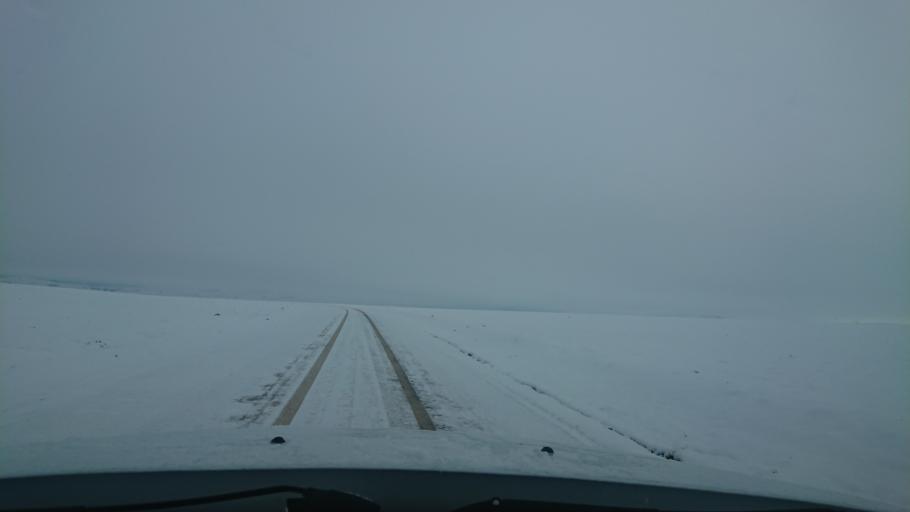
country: TR
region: Aksaray
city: Agacoren
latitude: 38.7443
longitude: 33.8747
